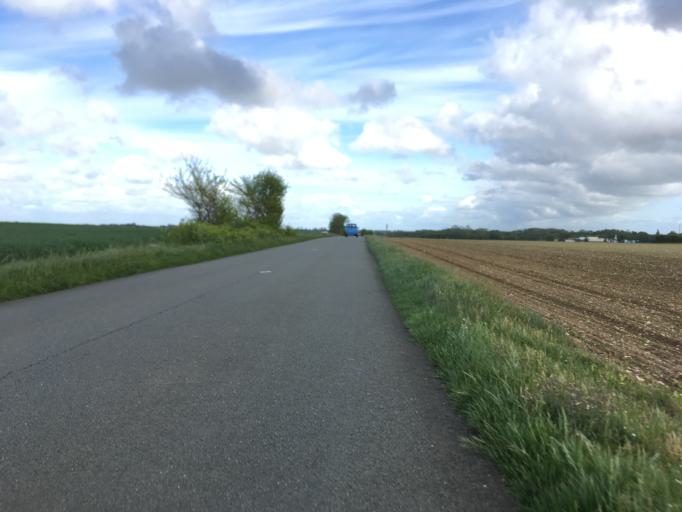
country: FR
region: Poitou-Charentes
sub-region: Departement de la Charente-Maritime
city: Verines
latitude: 46.1757
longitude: -0.9813
